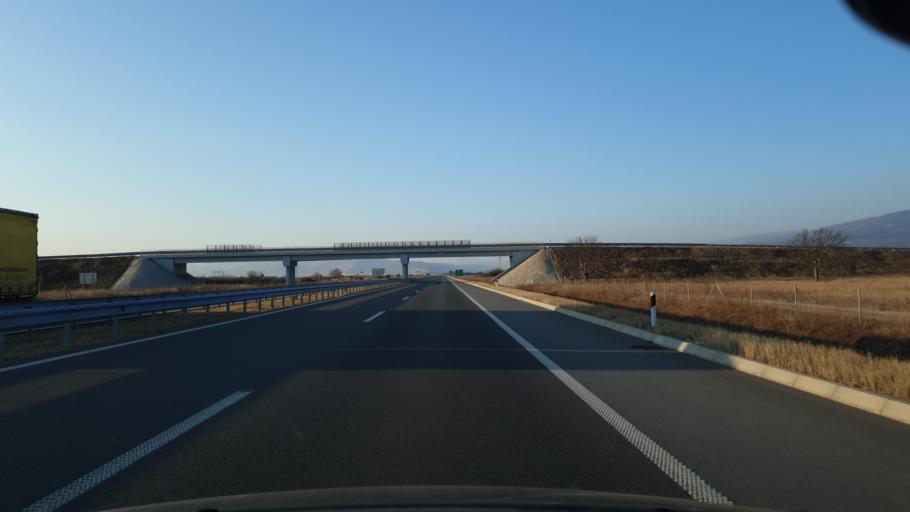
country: RS
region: Central Serbia
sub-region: Pirotski Okrug
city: Pirot
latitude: 43.1059
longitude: 22.6374
